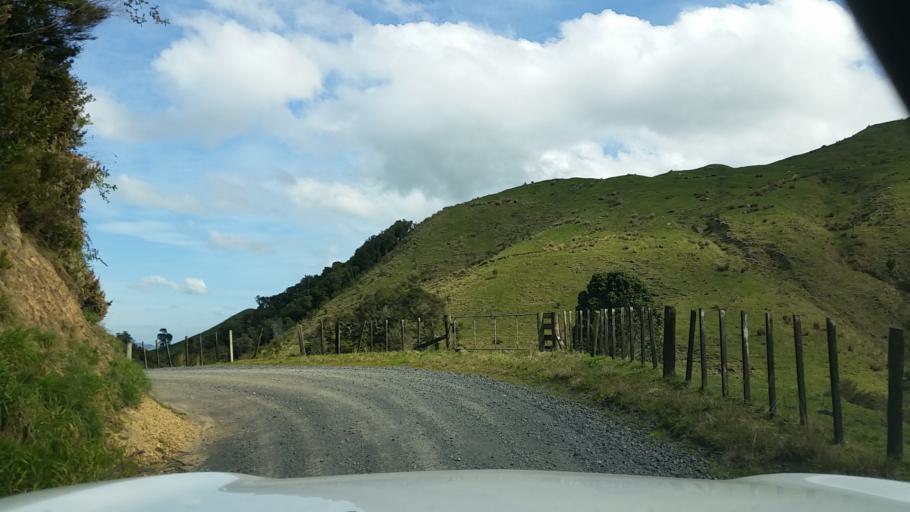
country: NZ
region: Waikato
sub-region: Hauraki District
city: Ngatea
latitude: -37.4761
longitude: 175.4560
